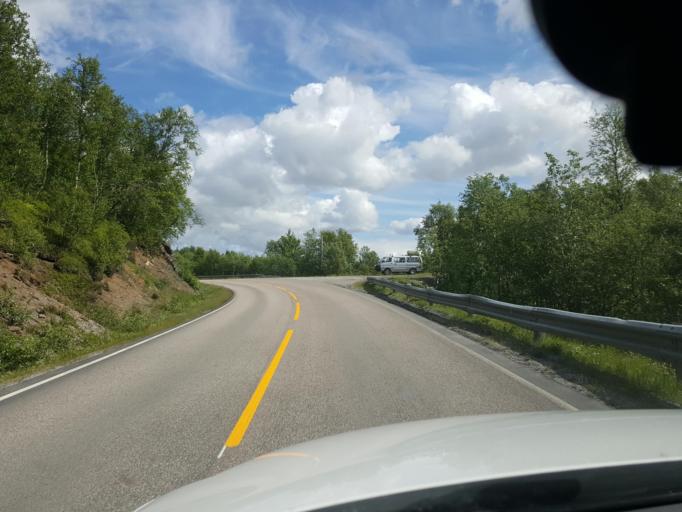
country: NO
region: Nordland
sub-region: Rana
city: Mo i Rana
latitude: 66.2878
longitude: 14.4275
